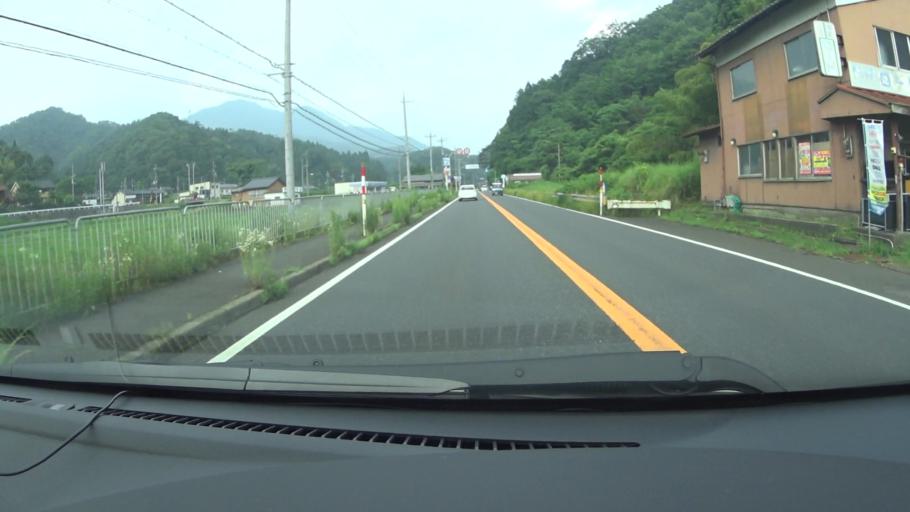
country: JP
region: Kyoto
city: Maizuru
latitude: 35.4843
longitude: 135.4495
